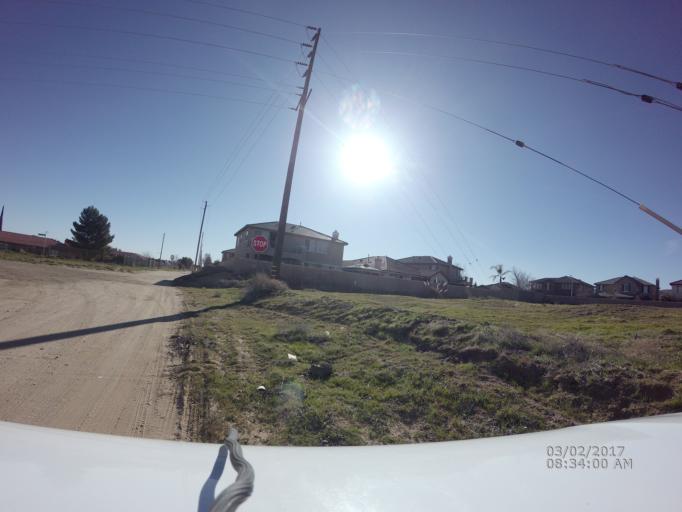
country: US
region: California
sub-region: Los Angeles County
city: Quartz Hill
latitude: 34.6236
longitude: -118.2014
